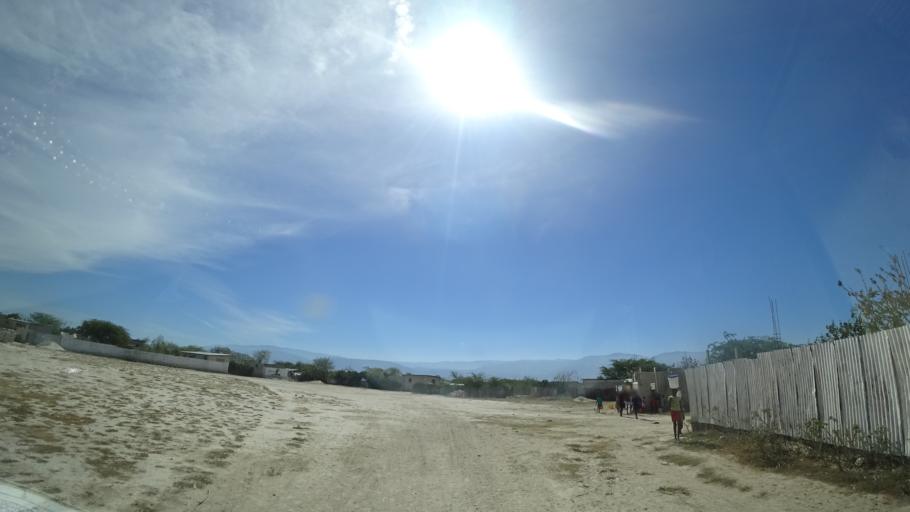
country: HT
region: Ouest
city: Croix des Bouquets
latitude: 18.6537
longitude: -72.2496
